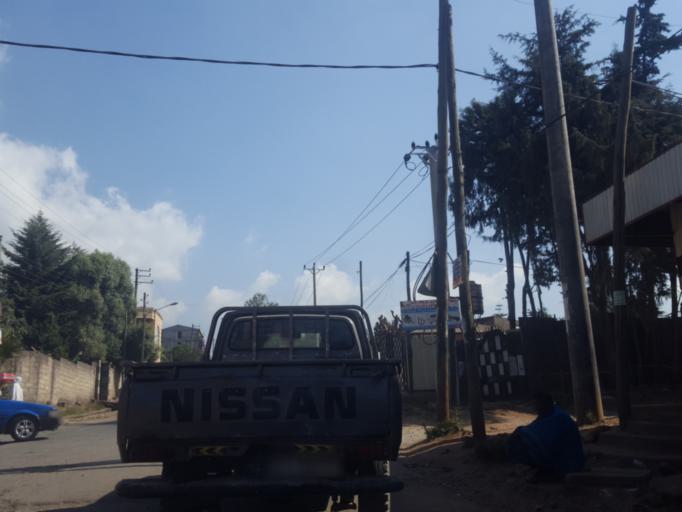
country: ET
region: Adis Abeba
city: Addis Ababa
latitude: 9.0504
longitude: 38.7275
